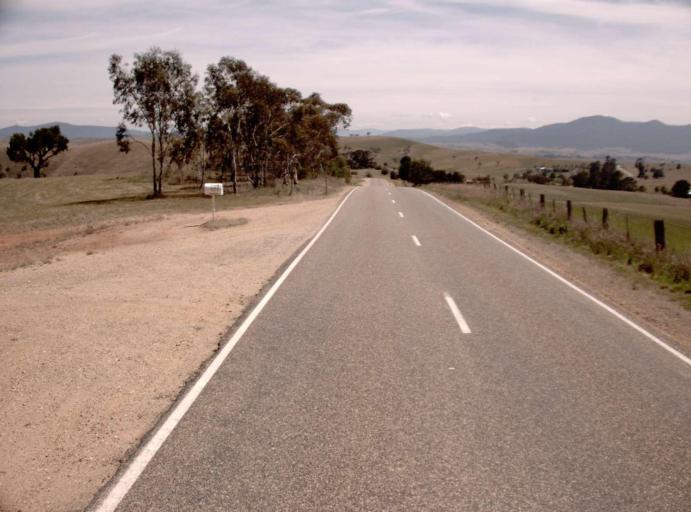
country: AU
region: Victoria
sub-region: Alpine
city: Mount Beauty
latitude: -37.0198
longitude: 147.6510
